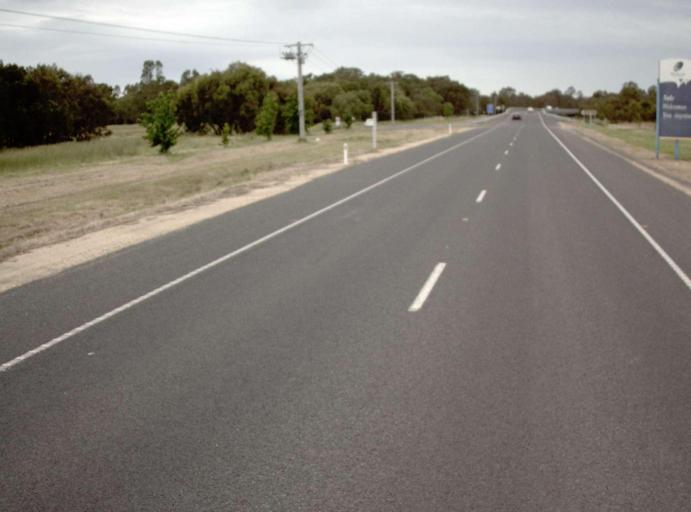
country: AU
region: Victoria
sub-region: Wellington
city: Sale
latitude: -38.1220
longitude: 147.0689
